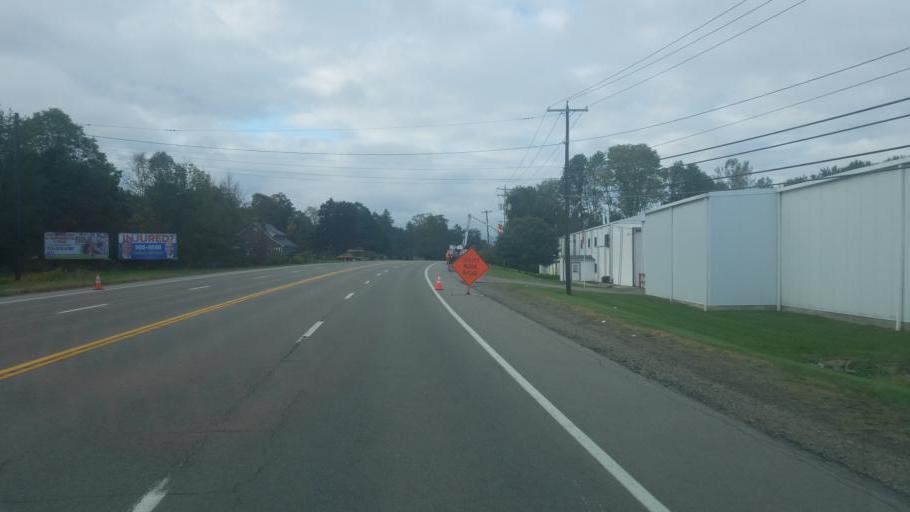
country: US
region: New York
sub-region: Cattaraugus County
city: Olean
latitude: 42.1373
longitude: -78.4023
